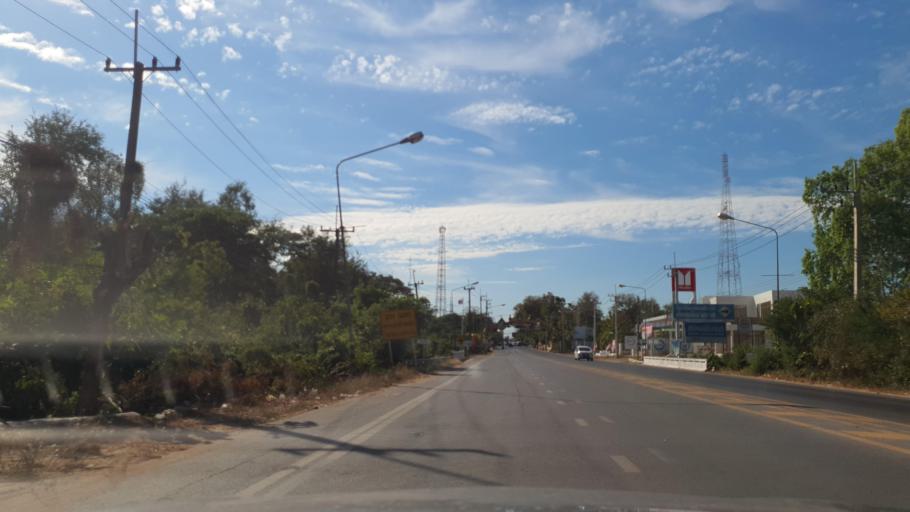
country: TH
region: Kalasin
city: Kuchinarai
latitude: 16.5378
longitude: 104.0584
